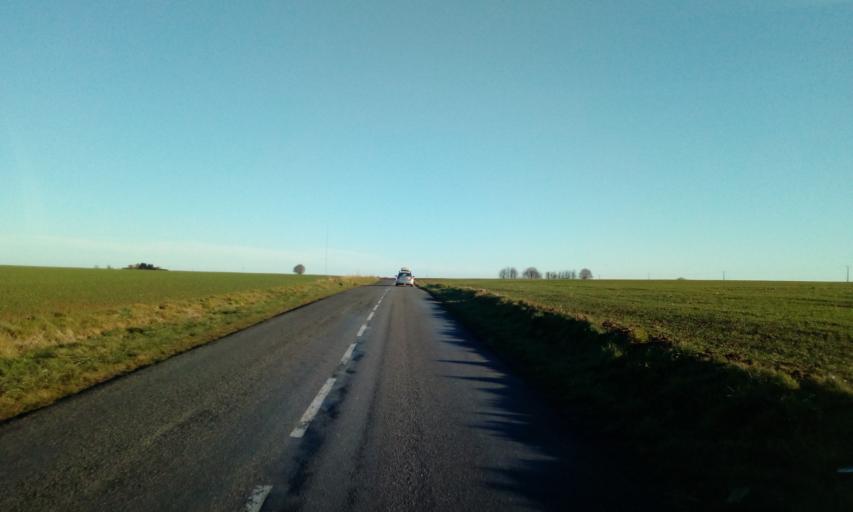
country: FR
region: Picardie
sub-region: Departement de l'Aisne
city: Rozoy-sur-Serre
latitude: 49.6978
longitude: 4.1658
